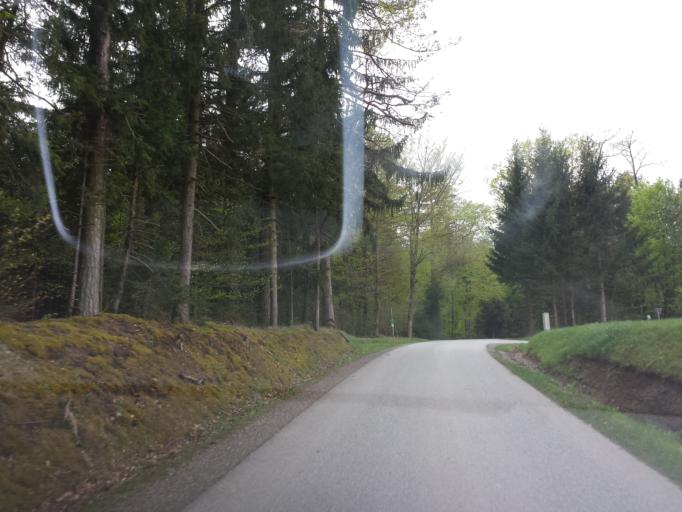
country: AT
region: Styria
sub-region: Politischer Bezirk Hartberg-Fuerstenfeld
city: Loipersdorf bei Fuerstenfeld
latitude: 47.0123
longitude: 16.1253
